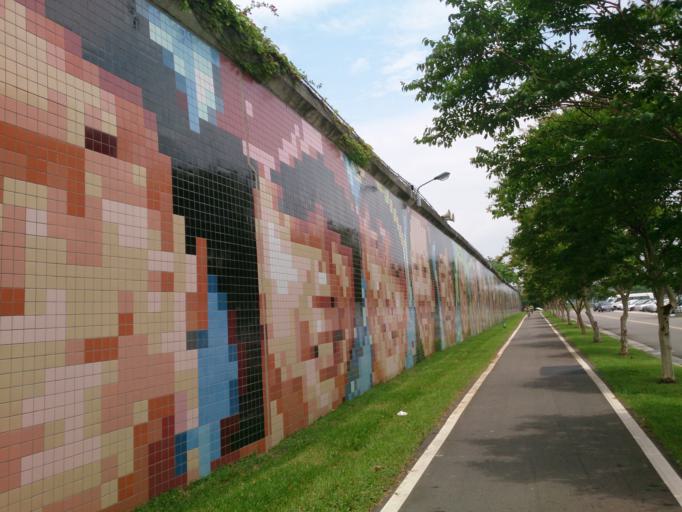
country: TW
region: Taipei
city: Taipei
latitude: 25.0740
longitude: 121.5363
